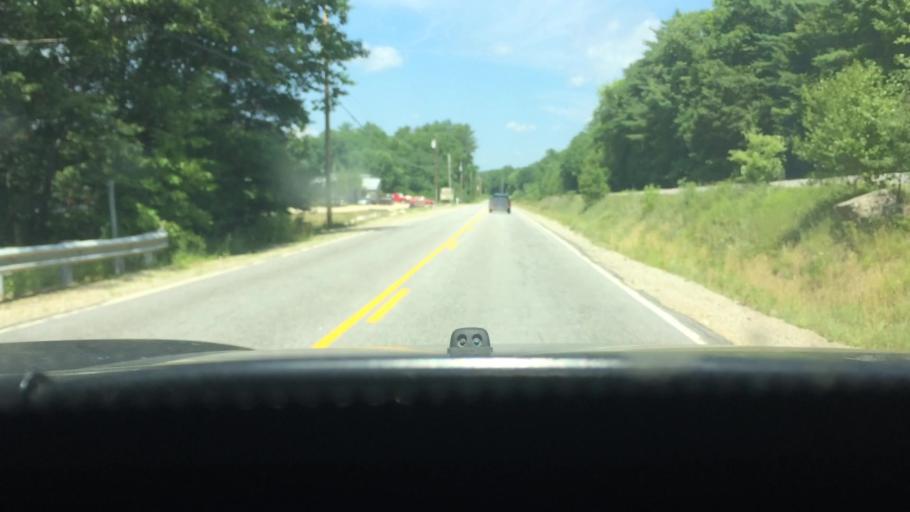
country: US
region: Maine
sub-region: Androscoggin County
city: Mechanic Falls
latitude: 44.1256
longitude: -70.4337
